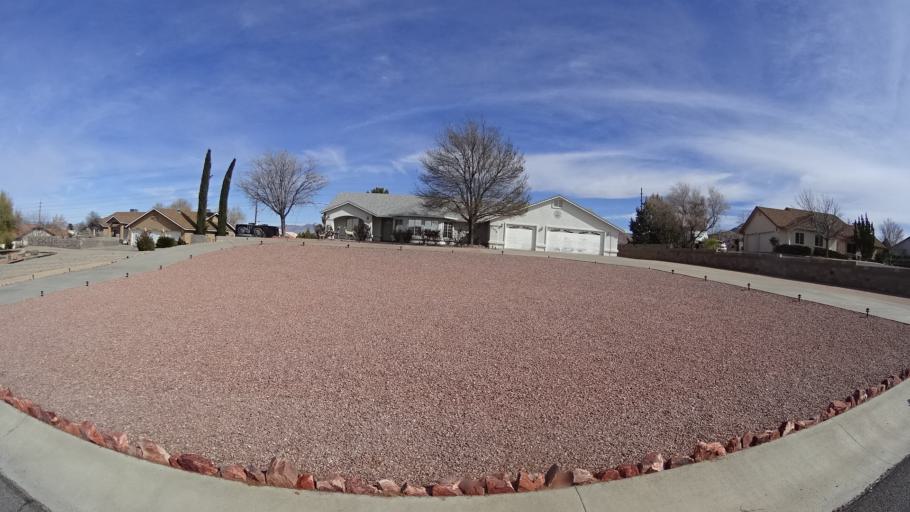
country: US
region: Arizona
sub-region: Mohave County
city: Kingman
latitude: 35.1925
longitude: -113.9876
